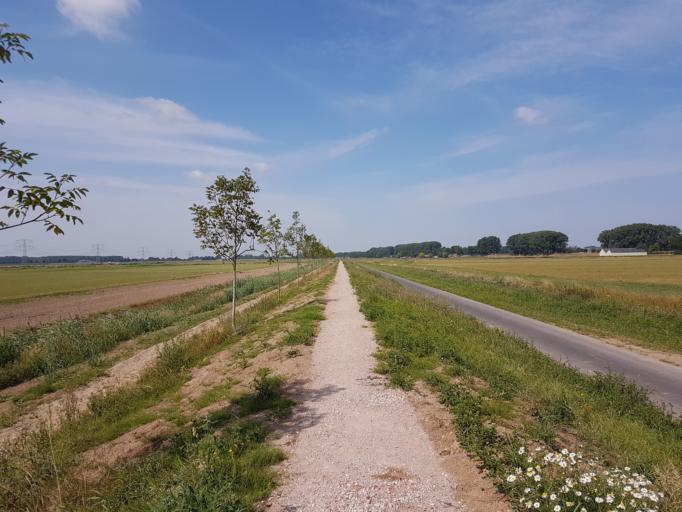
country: NL
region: South Holland
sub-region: Gemeente Dordrecht
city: Dordrecht
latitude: 51.7790
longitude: 4.7210
